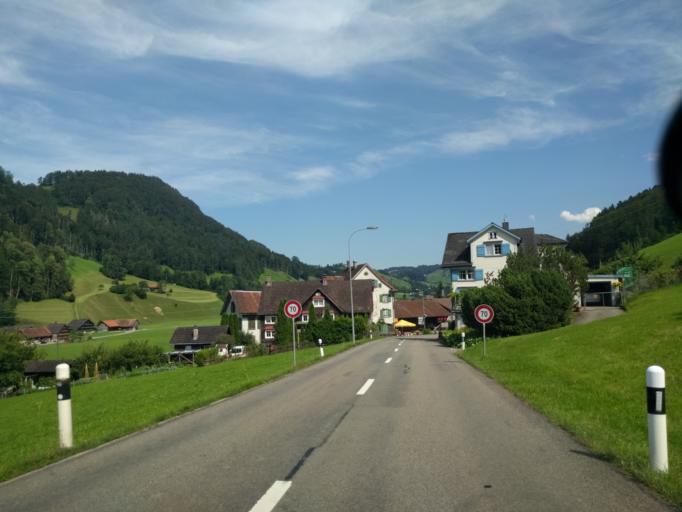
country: CH
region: Saint Gallen
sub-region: Wahlkreis Toggenburg
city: Mogelsberg
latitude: 47.3292
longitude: 9.1354
